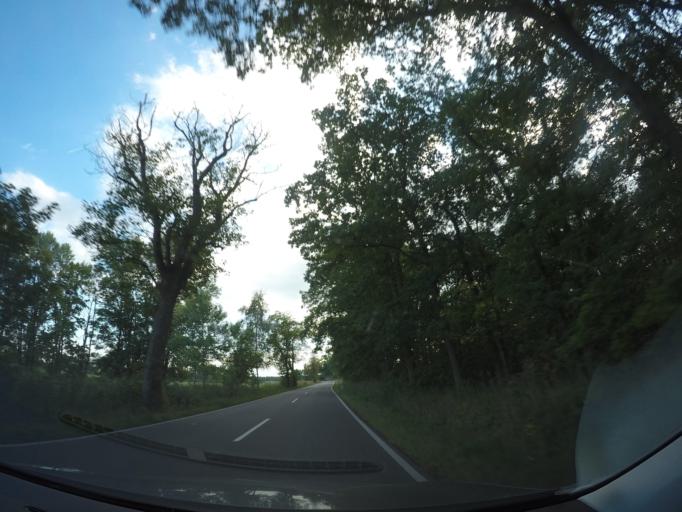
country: DE
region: Saxony-Anhalt
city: Kusey
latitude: 52.5509
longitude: 11.1398
